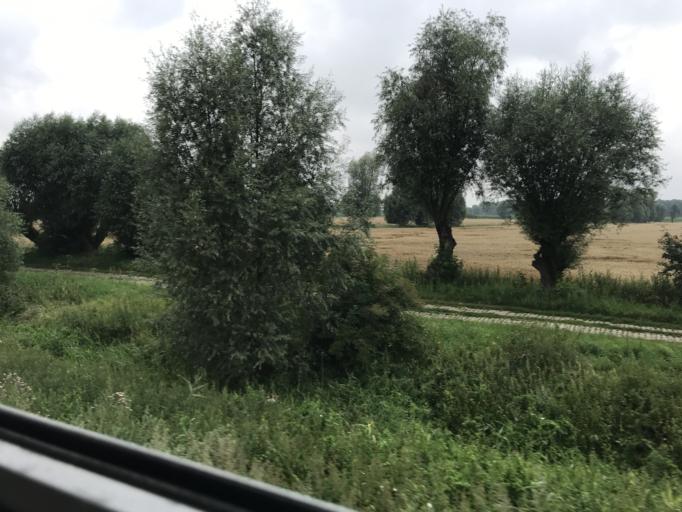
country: PL
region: Warmian-Masurian Voivodeship
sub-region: Powiat elblaski
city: Gronowo Elblaskie
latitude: 54.0992
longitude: 19.3254
